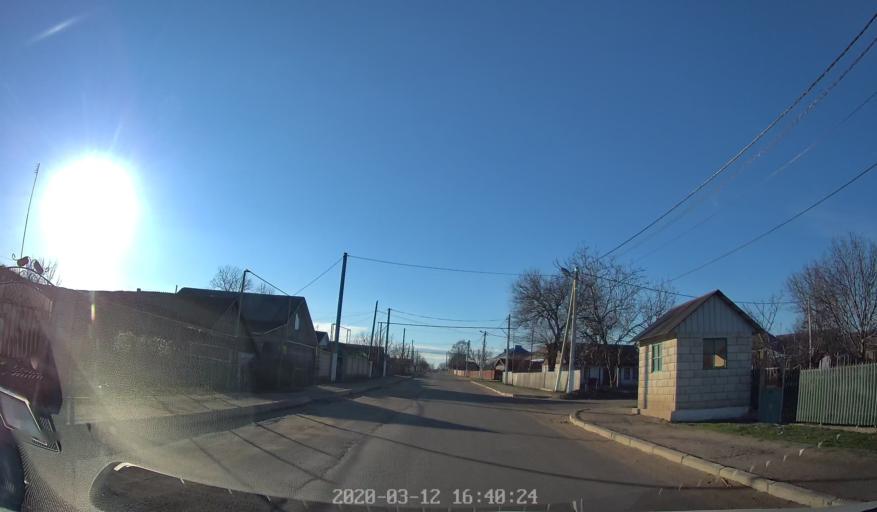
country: MD
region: Anenii Noi
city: Anenii Noi
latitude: 46.8179
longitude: 29.1485
